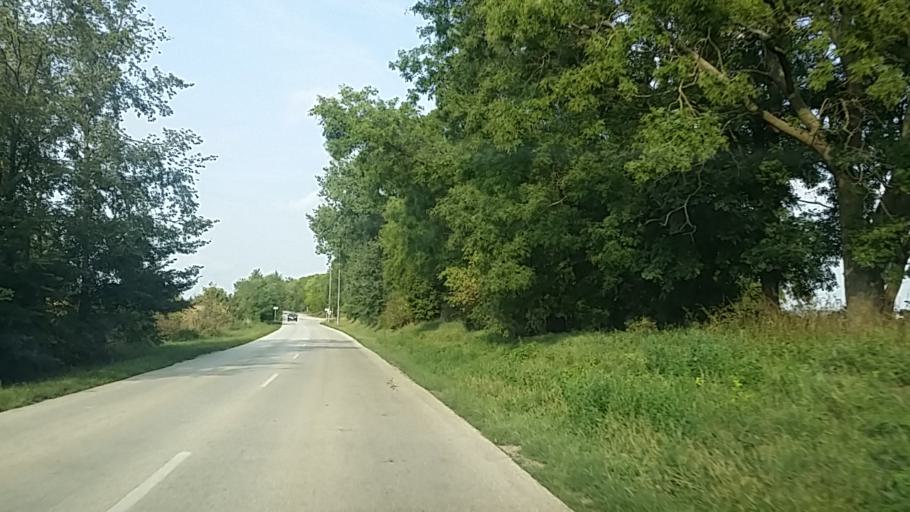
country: HU
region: Komarom-Esztergom
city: Tata
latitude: 47.6322
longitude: 18.2908
